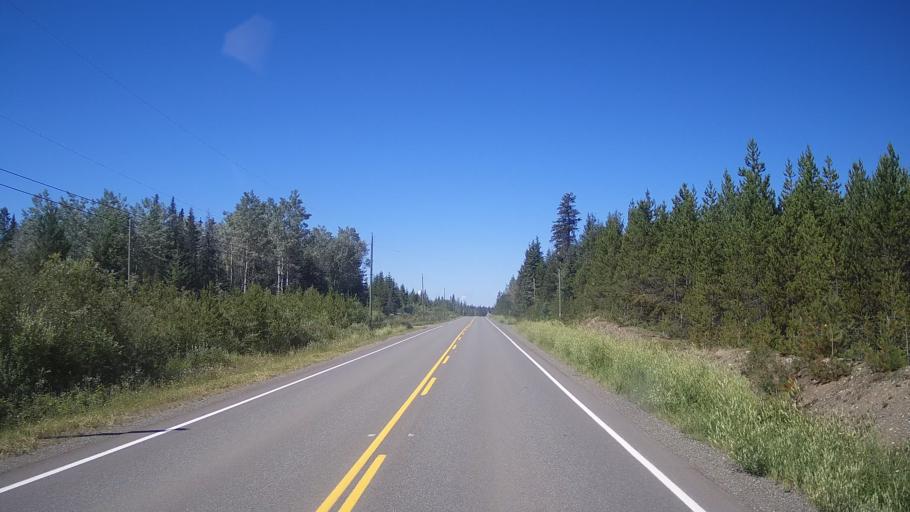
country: CA
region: British Columbia
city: Cache Creek
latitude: 51.5405
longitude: -120.9747
